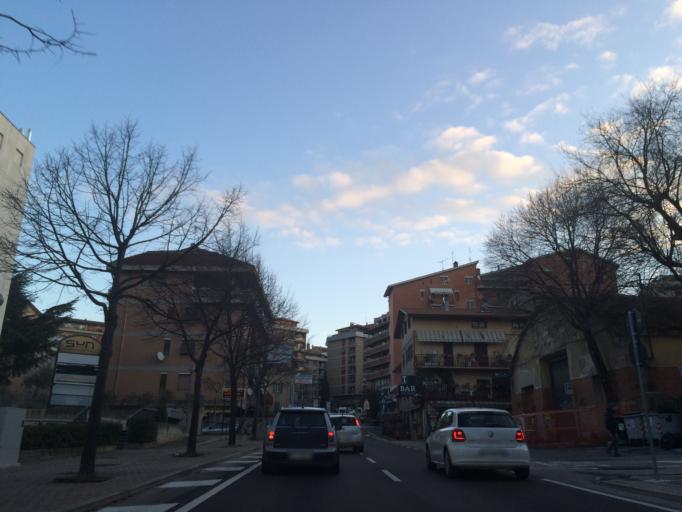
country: IT
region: Umbria
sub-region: Provincia di Perugia
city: Perugia
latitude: 43.0969
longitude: 12.3864
